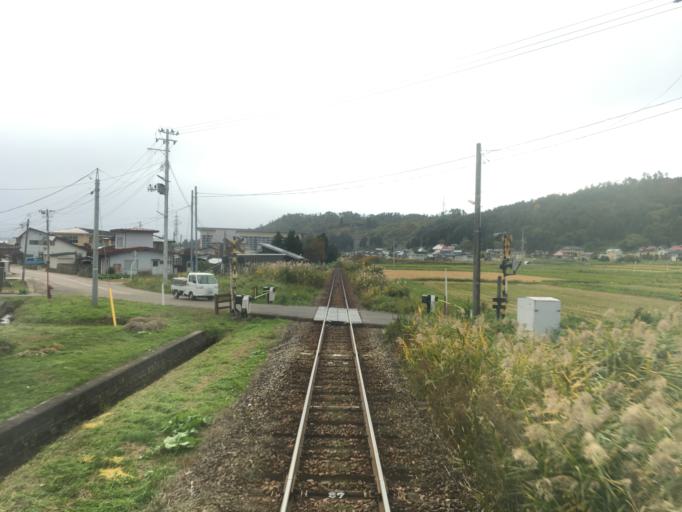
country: JP
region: Yamagata
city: Nagai
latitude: 38.0579
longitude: 140.1032
